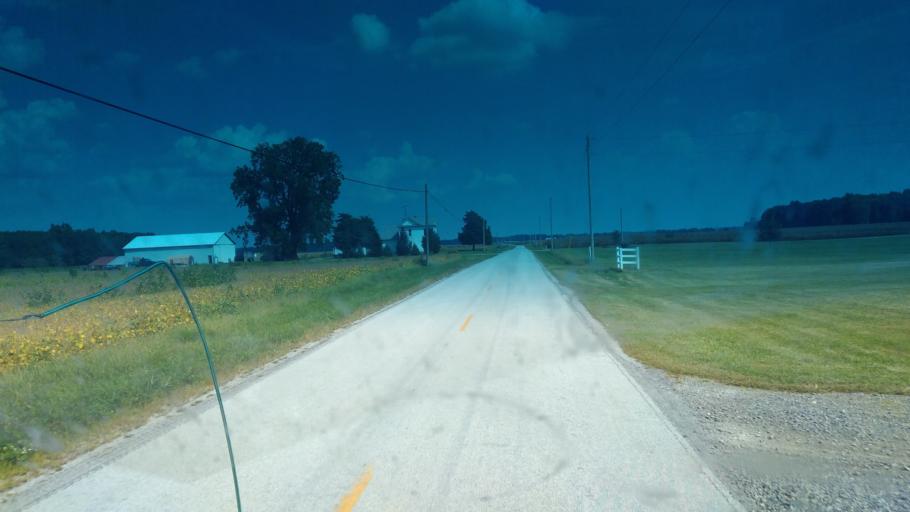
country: US
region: Ohio
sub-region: Hardin County
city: Kenton
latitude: 40.6421
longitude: -83.6749
